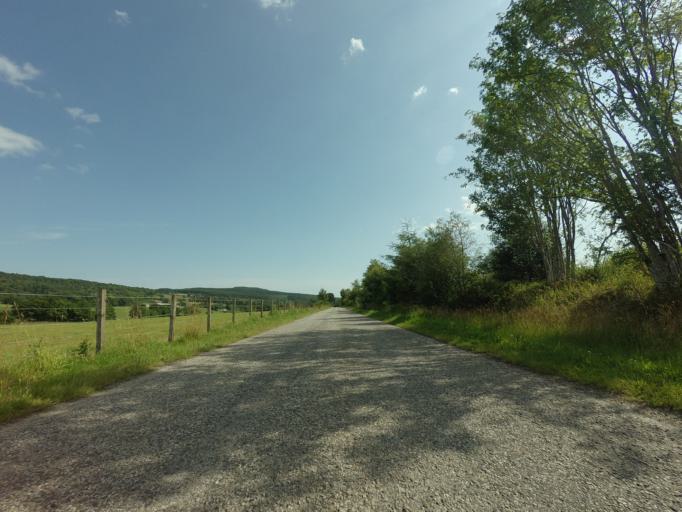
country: GB
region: Scotland
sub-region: Highland
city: Invergordon
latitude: 57.7482
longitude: -4.1652
